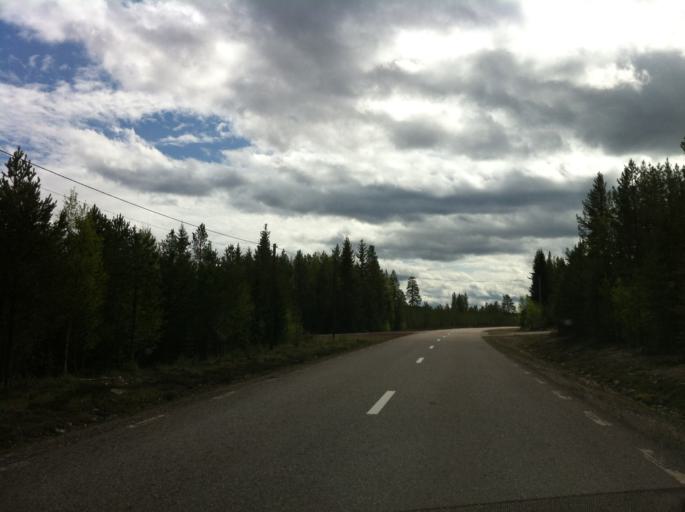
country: NO
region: Hedmark
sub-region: Trysil
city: Innbygda
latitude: 61.6307
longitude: 13.1354
